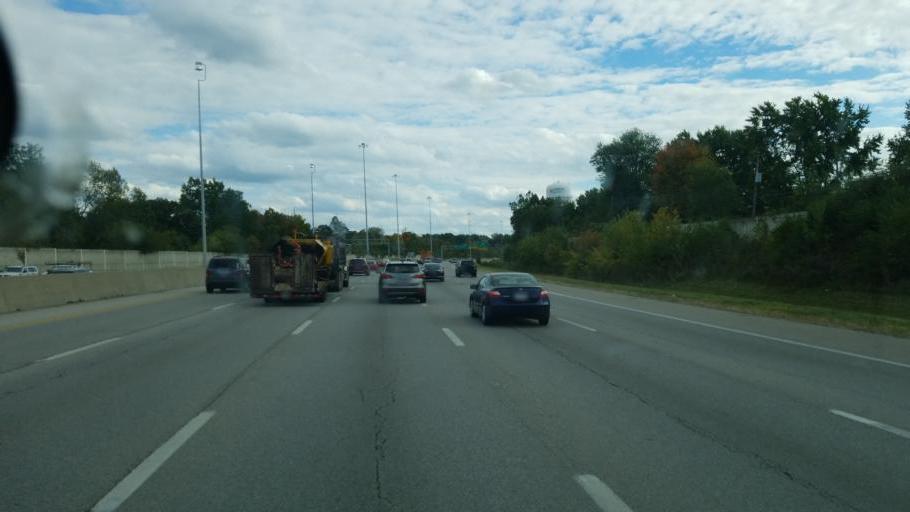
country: US
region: Ohio
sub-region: Franklin County
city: Huber Ridge
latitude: 40.0942
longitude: -82.9099
